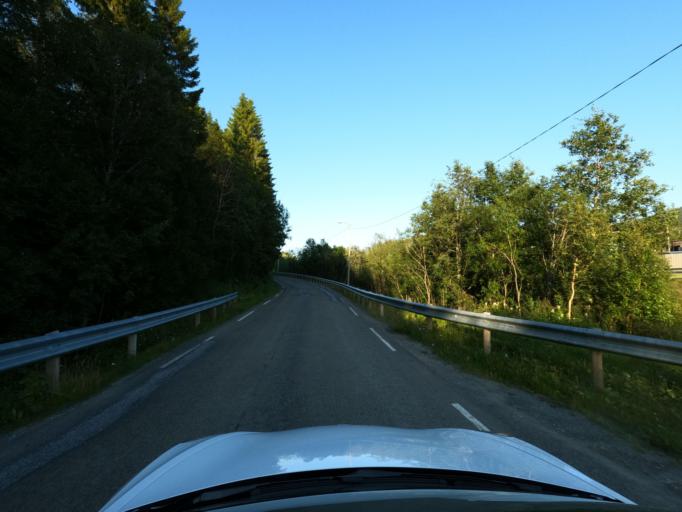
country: NO
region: Nordland
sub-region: Ballangen
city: Ballangen
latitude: 68.4928
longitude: 16.7315
